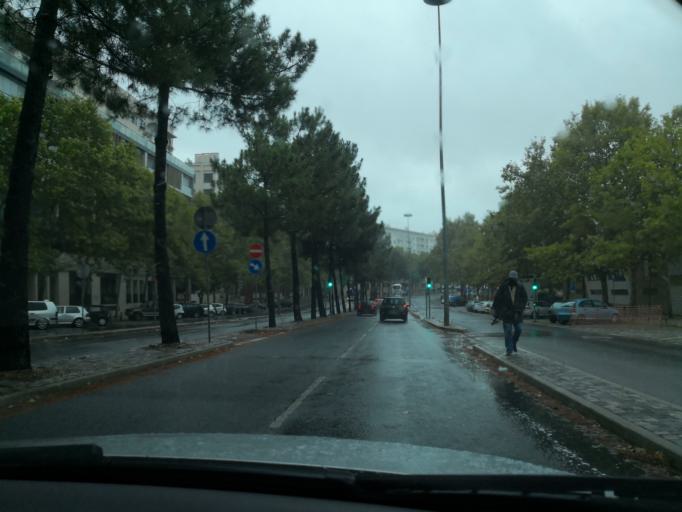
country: PT
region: Lisbon
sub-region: Loures
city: Moscavide
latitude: 38.7791
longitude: -9.0979
